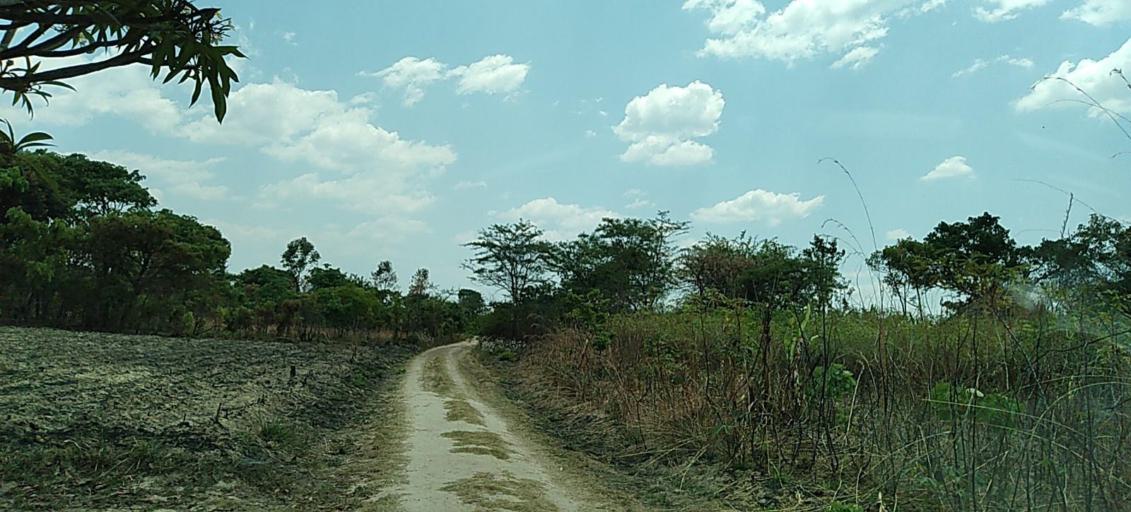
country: ZM
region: Copperbelt
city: Chililabombwe
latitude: -12.4598
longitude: 27.6699
